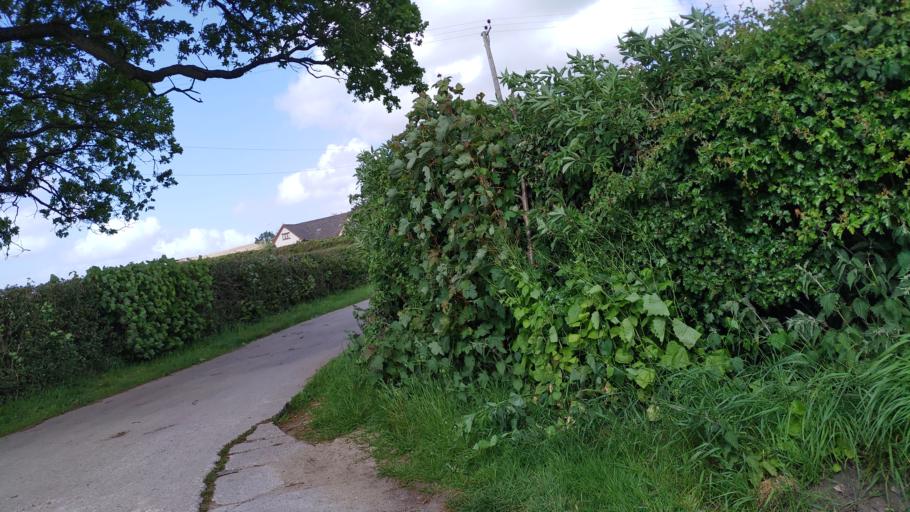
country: GB
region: England
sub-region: Lancashire
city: Chorley
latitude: 53.6431
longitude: -2.5891
